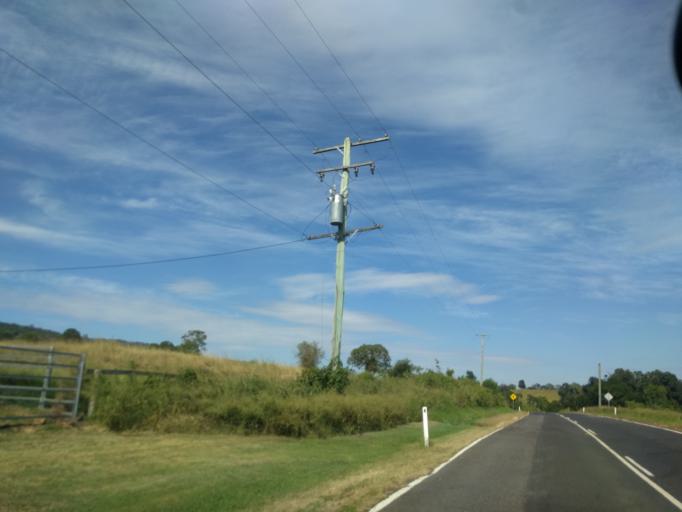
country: AU
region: Queensland
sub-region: Ipswich
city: Thagoona
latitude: -27.5929
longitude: 152.5534
